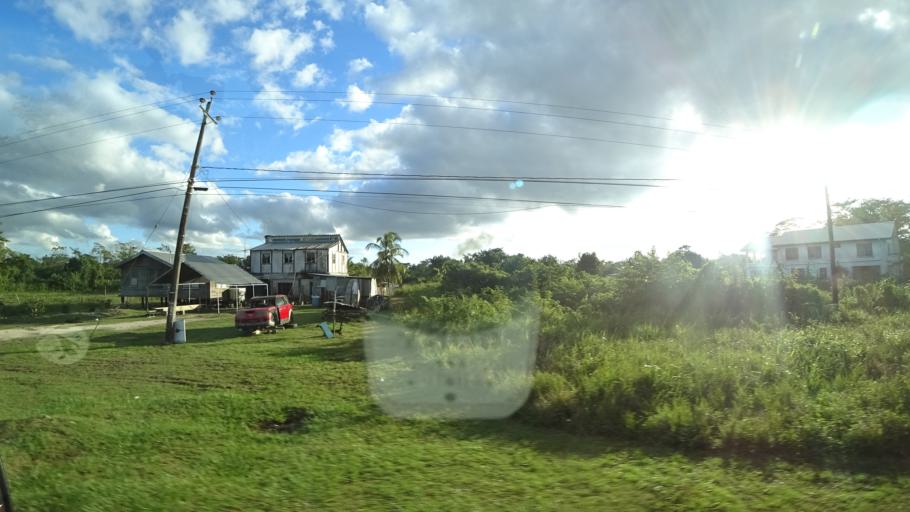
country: BZ
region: Belize
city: Belize City
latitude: 17.5716
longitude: -88.3905
